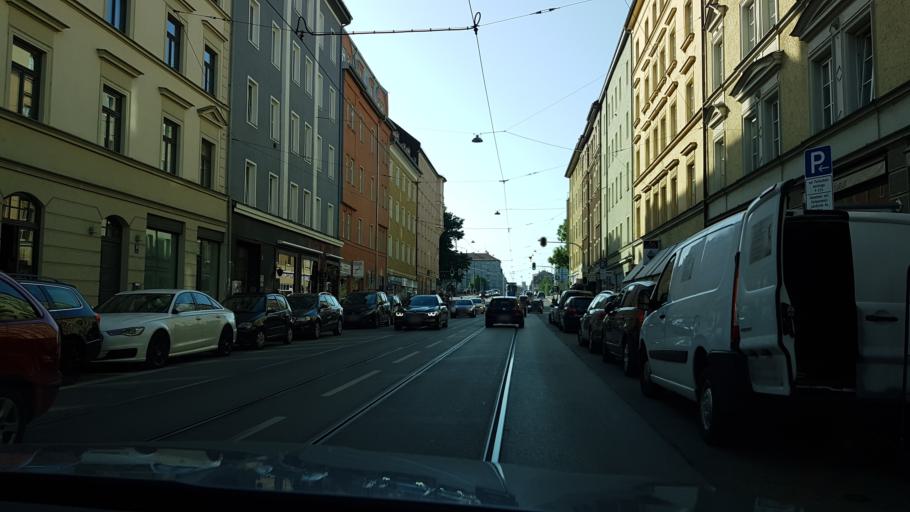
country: DE
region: Bavaria
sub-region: Upper Bavaria
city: Munich
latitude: 48.1258
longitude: 11.5791
